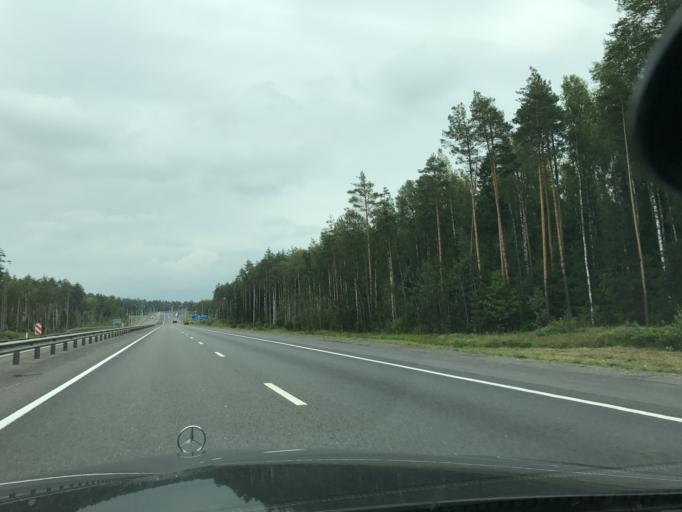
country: RU
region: Vladimir
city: Kameshkovo
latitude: 56.1866
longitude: 40.9492
